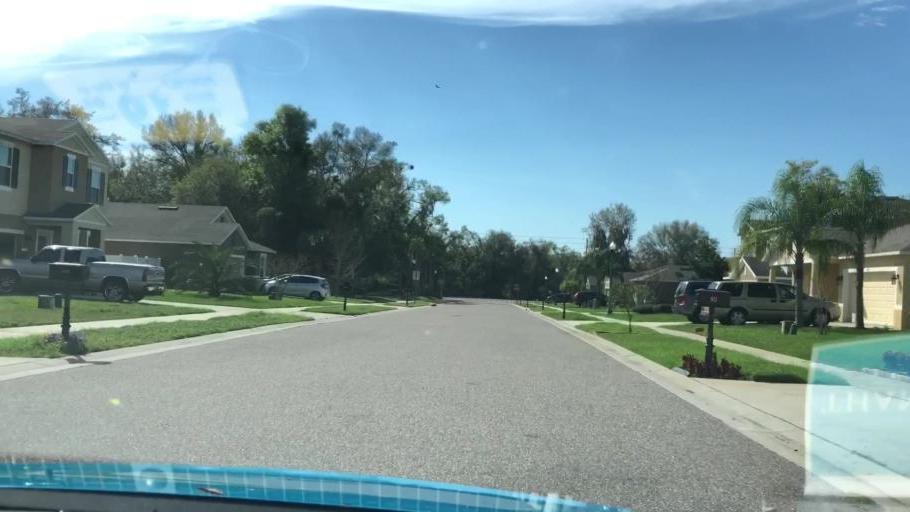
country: US
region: Florida
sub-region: Volusia County
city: Deltona
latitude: 28.8708
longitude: -81.2496
